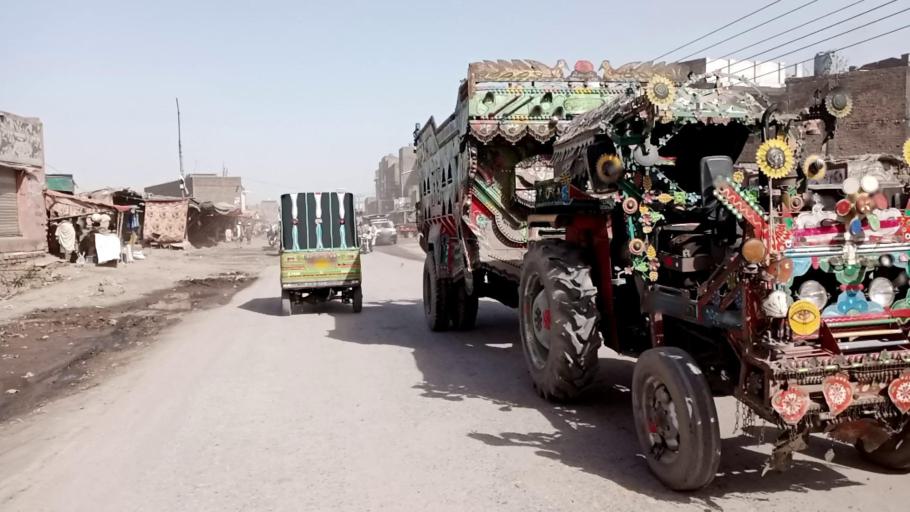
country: PK
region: Khyber Pakhtunkhwa
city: Peshawar
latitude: 33.9914
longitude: 71.6335
